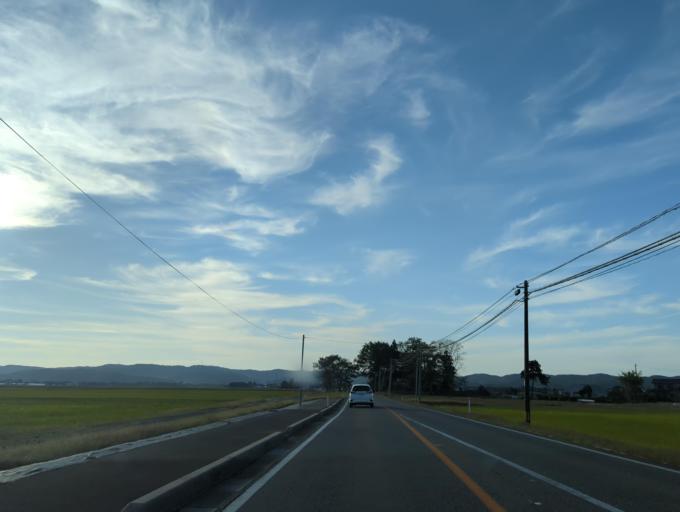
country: JP
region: Niigata
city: Mitsuke
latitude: 37.5551
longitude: 138.8478
